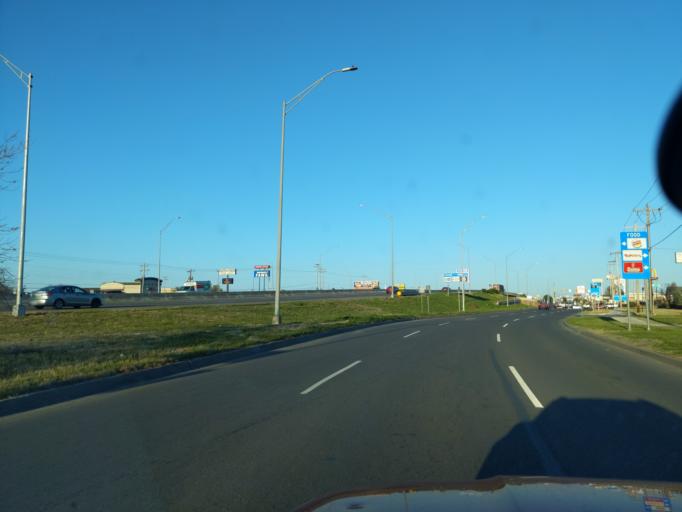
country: US
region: Oklahoma
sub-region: Cleveland County
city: Moore
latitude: 35.3911
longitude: -97.5324
